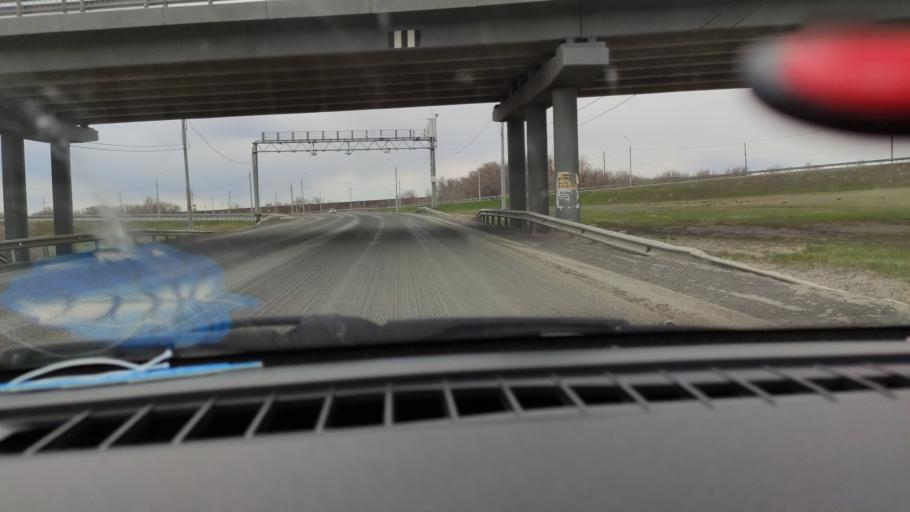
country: RU
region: Saratov
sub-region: Saratovskiy Rayon
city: Saratov
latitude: 51.7724
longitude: 46.0852
